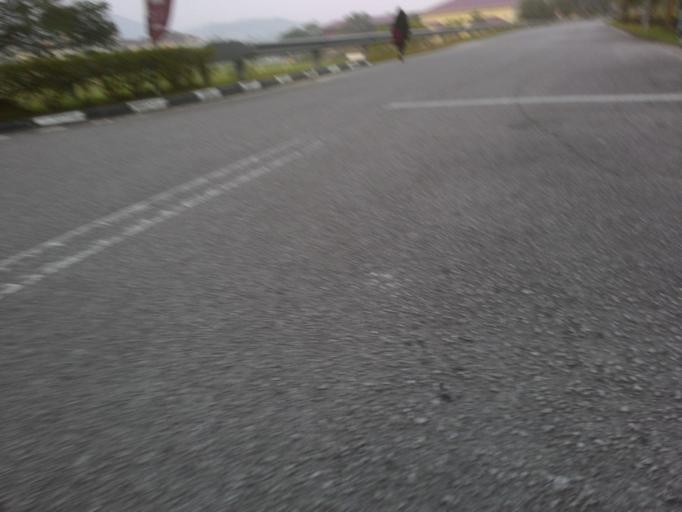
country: MY
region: Kedah
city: Kulim
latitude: 5.3828
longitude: 100.5785
